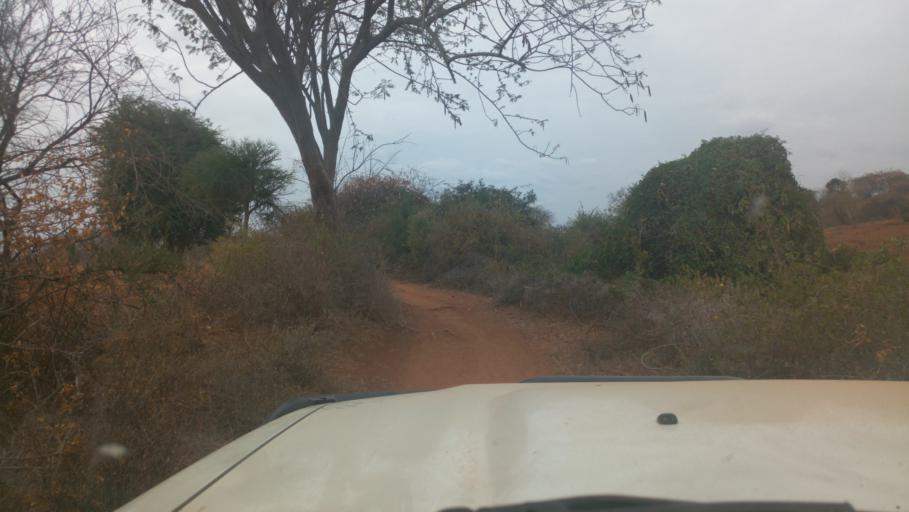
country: KE
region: Makueni
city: Makueni
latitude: -1.9699
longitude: 38.0775
